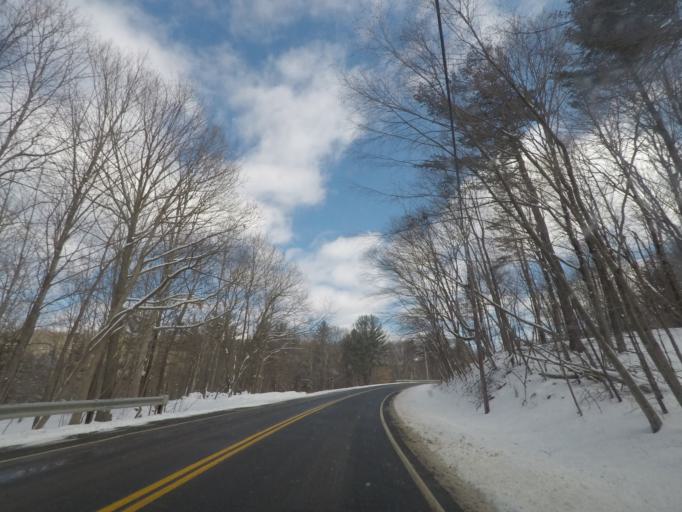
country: US
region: New York
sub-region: Rensselaer County
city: Nassau
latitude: 42.4700
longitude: -73.5322
